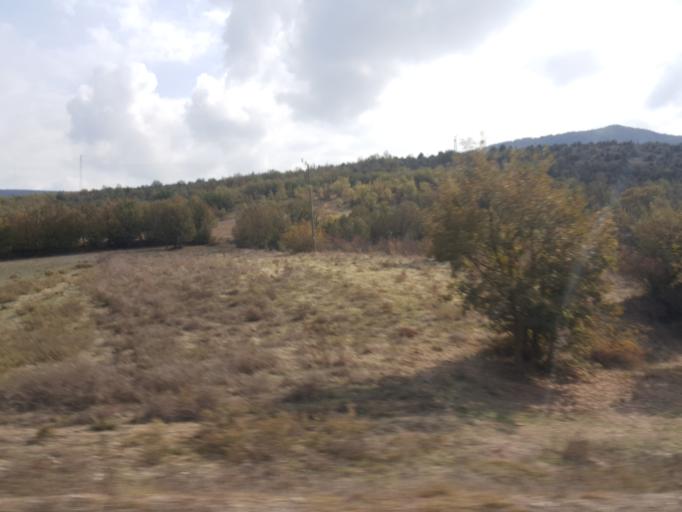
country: TR
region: Sinop
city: Sarayduzu
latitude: 41.3723
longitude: 34.8994
